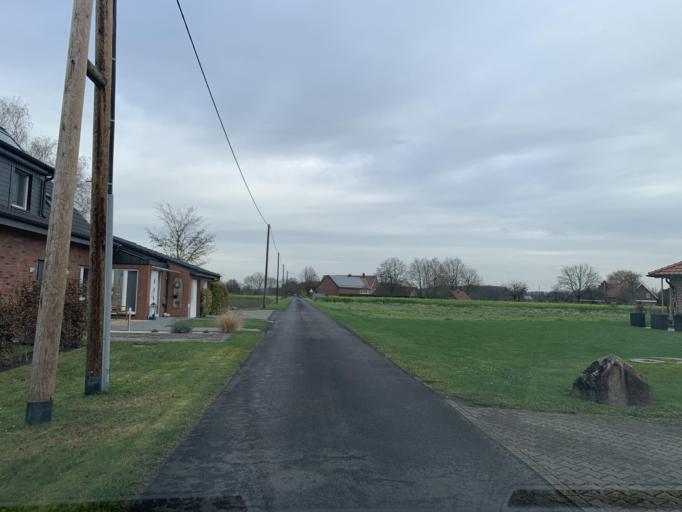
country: DE
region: North Rhine-Westphalia
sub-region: Regierungsbezirk Munster
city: Ascheberg
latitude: 51.8112
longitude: 7.6321
